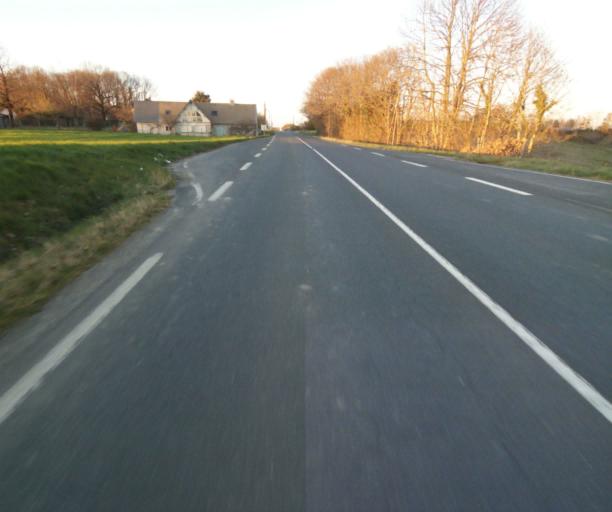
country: FR
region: Limousin
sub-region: Departement de la Correze
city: Sainte-Fereole
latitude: 45.2834
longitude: 1.5662
